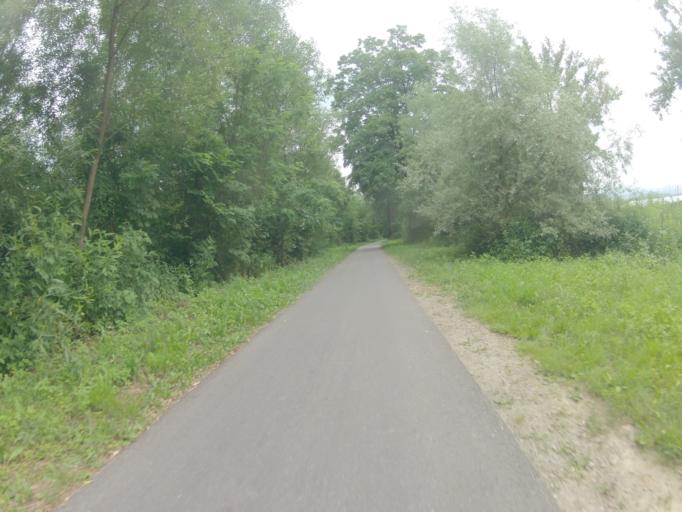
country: PL
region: Lesser Poland Voivodeship
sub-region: Powiat nowosadecki
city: Stary Sacz
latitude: 49.5391
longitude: 20.6577
